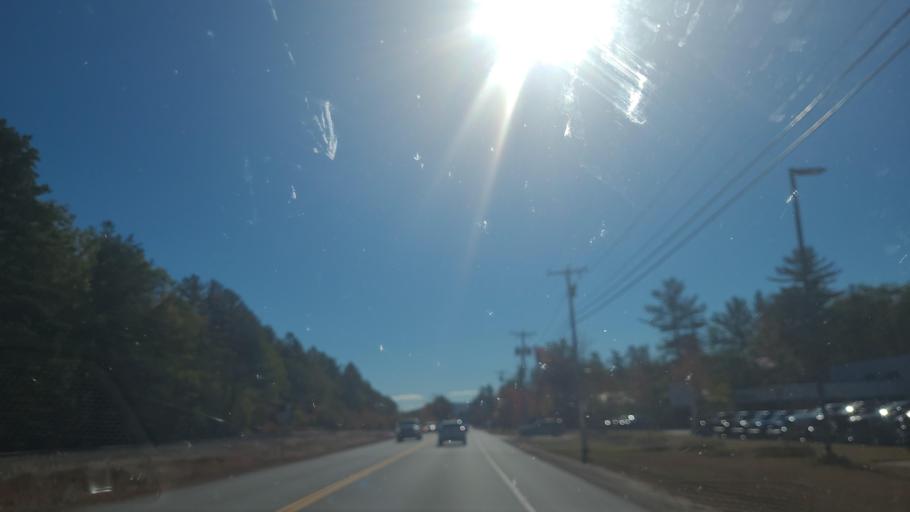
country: US
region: New Hampshire
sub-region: Carroll County
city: Conway
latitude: 44.0118
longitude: -71.0980
